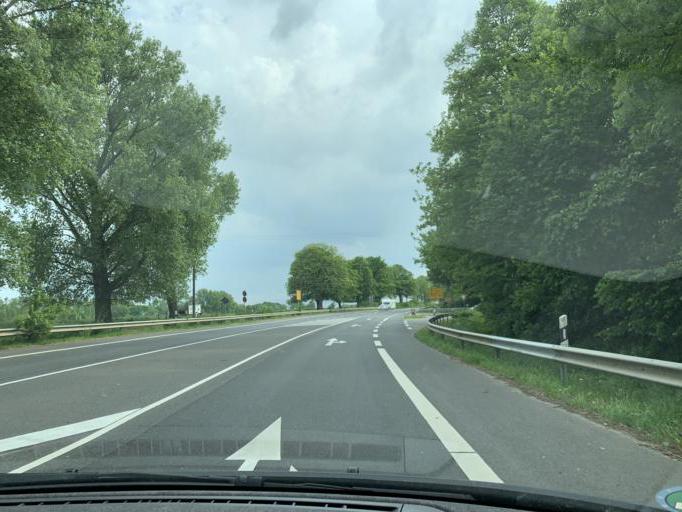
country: DE
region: North Rhine-Westphalia
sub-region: Regierungsbezirk Koln
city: Norvenich
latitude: 50.7969
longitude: 6.6362
